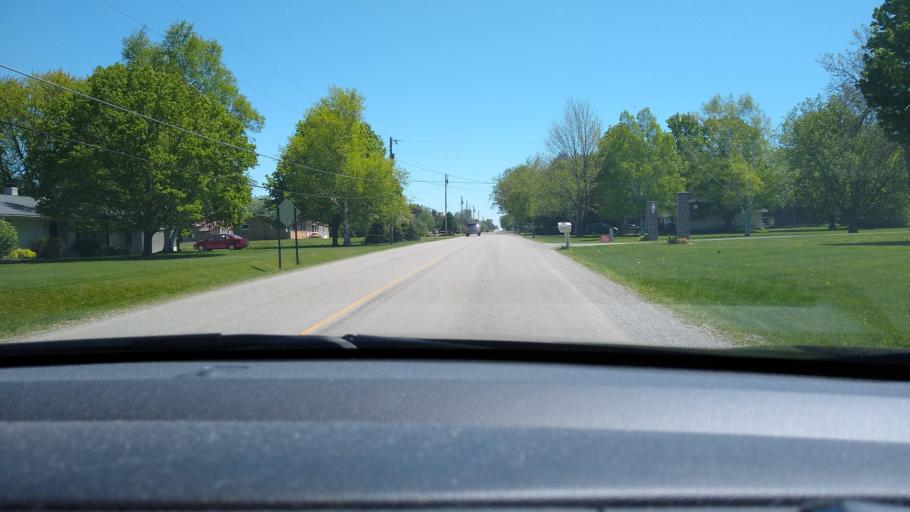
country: US
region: Michigan
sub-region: Delta County
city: Escanaba
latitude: 45.8260
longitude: -87.1817
